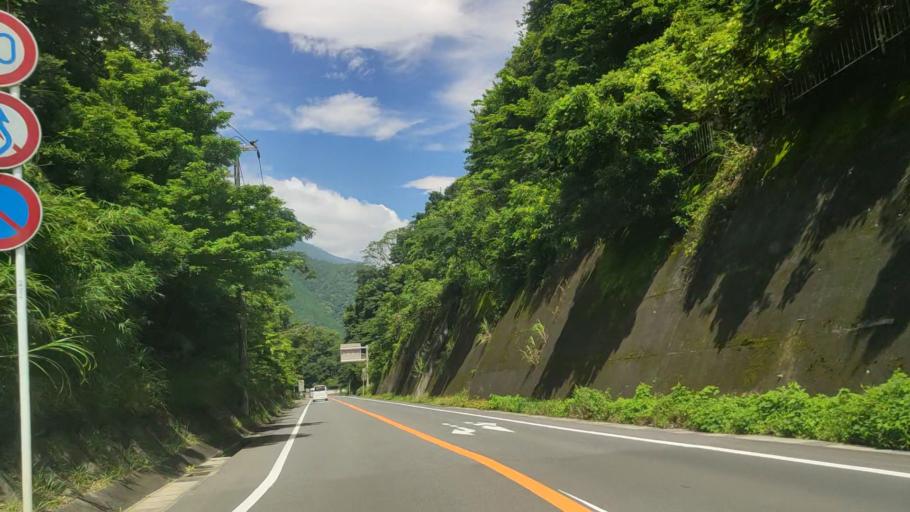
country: JP
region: Shizuoka
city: Fujinomiya
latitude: 35.3539
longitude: 138.4521
